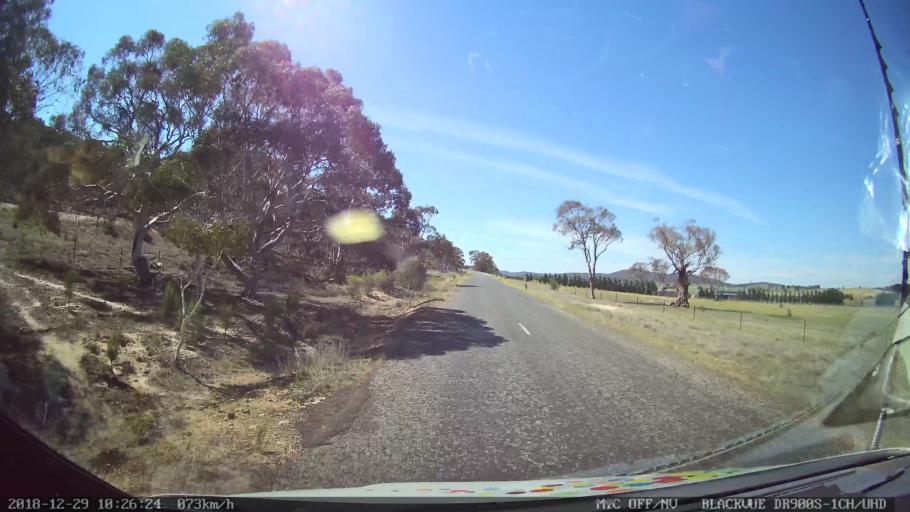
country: AU
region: New South Wales
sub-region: Yass Valley
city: Gundaroo
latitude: -34.9256
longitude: 149.4432
